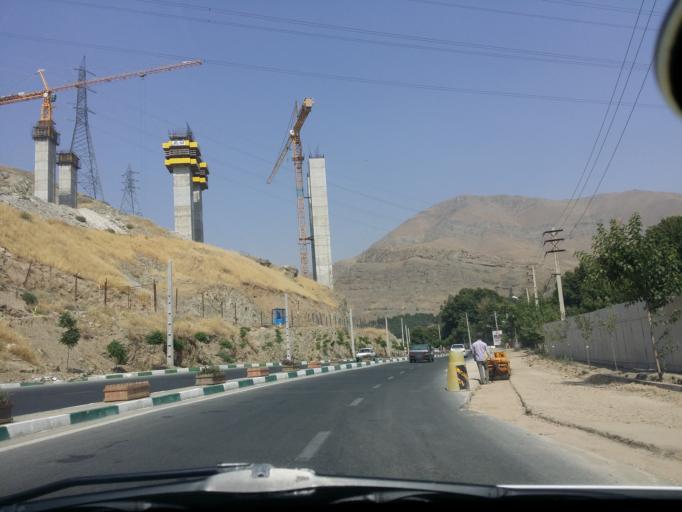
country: IR
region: Alborz
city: Karaj
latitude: 35.8309
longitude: 51.0343
